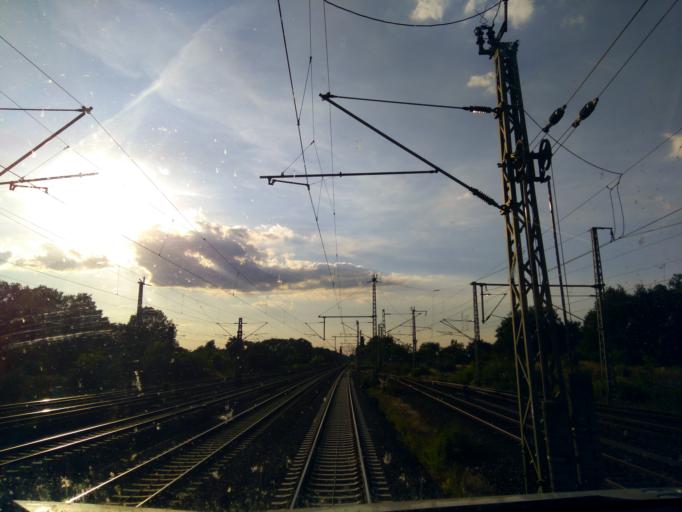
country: DE
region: Mecklenburg-Vorpommern
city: Ludwigslust
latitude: 53.3394
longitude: 11.4850
